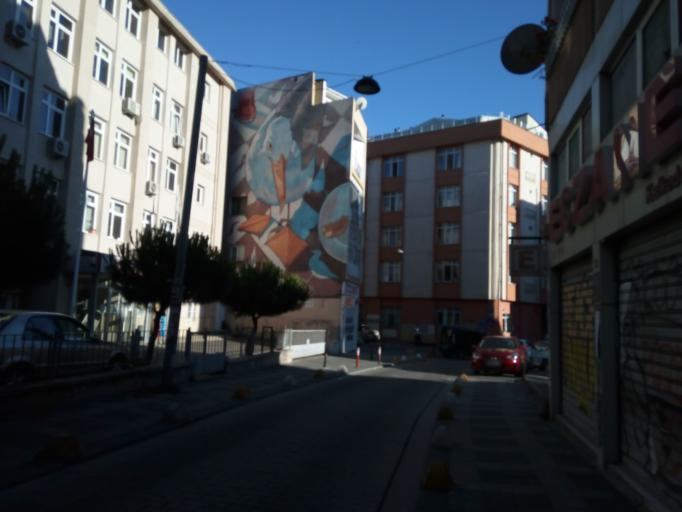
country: TR
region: Istanbul
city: UEskuedar
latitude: 40.9933
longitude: 29.0289
